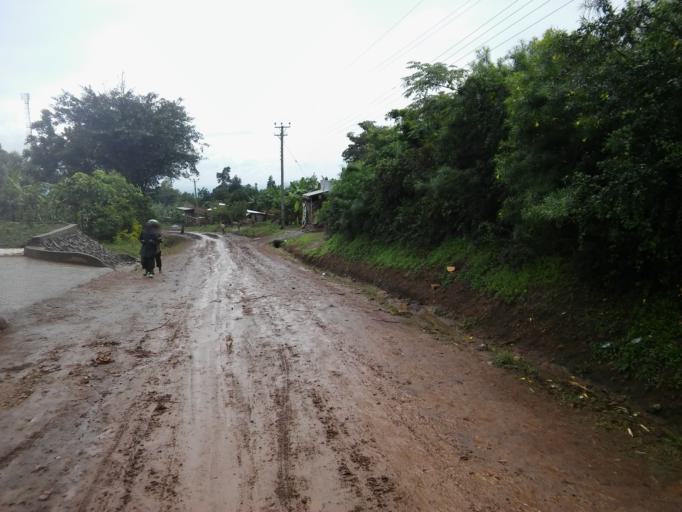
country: UG
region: Eastern Region
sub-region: Mbale District
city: Mbale
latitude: 1.0375
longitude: 34.2064
